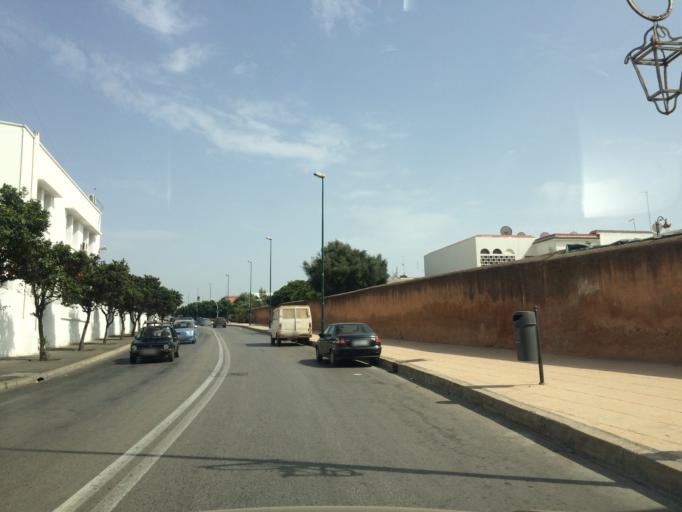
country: MA
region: Rabat-Sale-Zemmour-Zaer
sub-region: Rabat
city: Rabat
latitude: 34.0097
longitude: -6.8303
